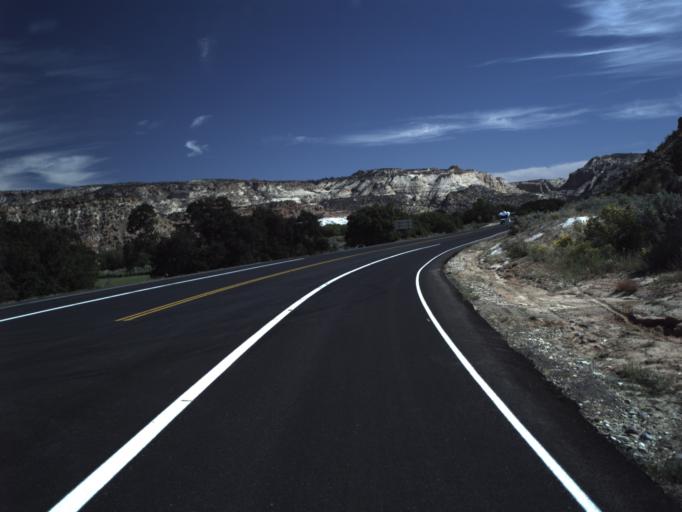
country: US
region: Utah
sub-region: Wayne County
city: Loa
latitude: 37.7772
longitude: -111.6287
